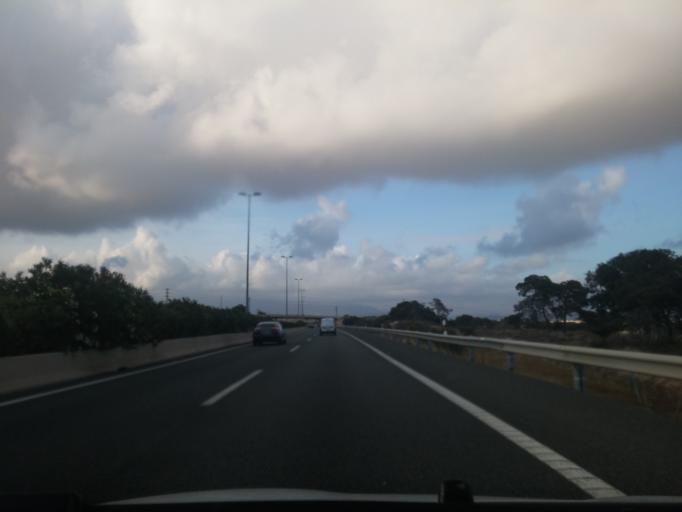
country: ES
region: Valencia
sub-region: Provincia de Alicante
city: San Juan de Alicante
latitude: 38.3895
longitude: -0.4531
